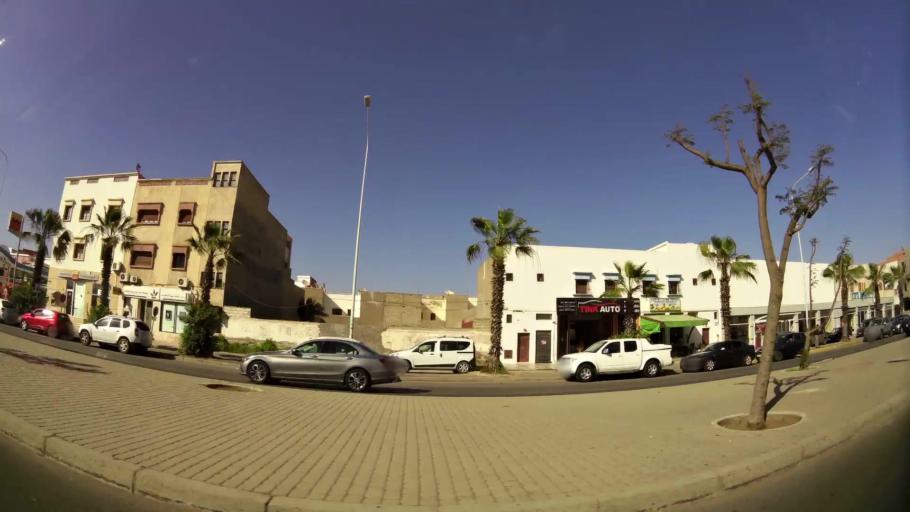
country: MA
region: Oued ed Dahab-Lagouira
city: Dakhla
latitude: 30.4098
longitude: -9.5595
